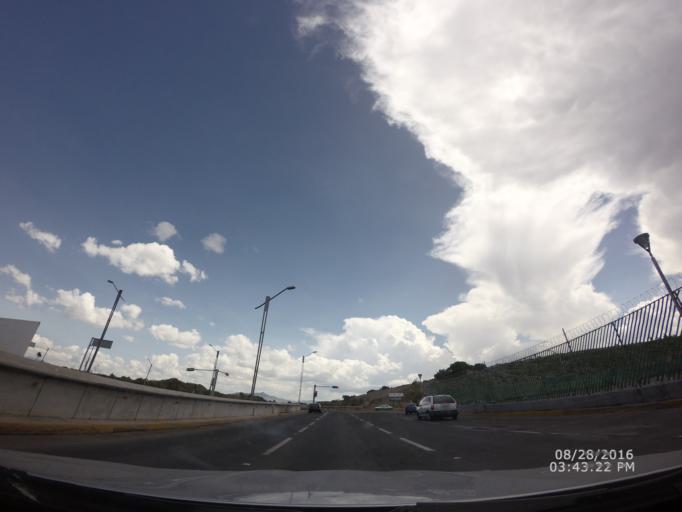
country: MX
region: Hidalgo
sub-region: Mineral de la Reforma
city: PRI Chacon
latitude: 20.0829
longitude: -98.7511
